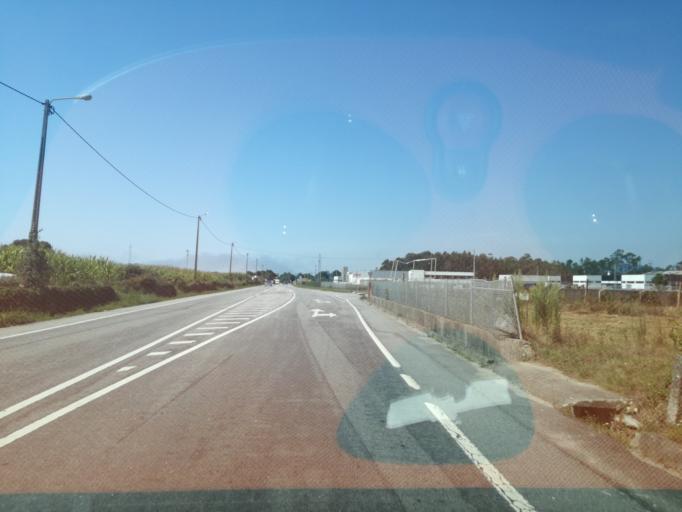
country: PT
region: Braga
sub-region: Esposende
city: Apulia
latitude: 41.4982
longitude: -8.7580
